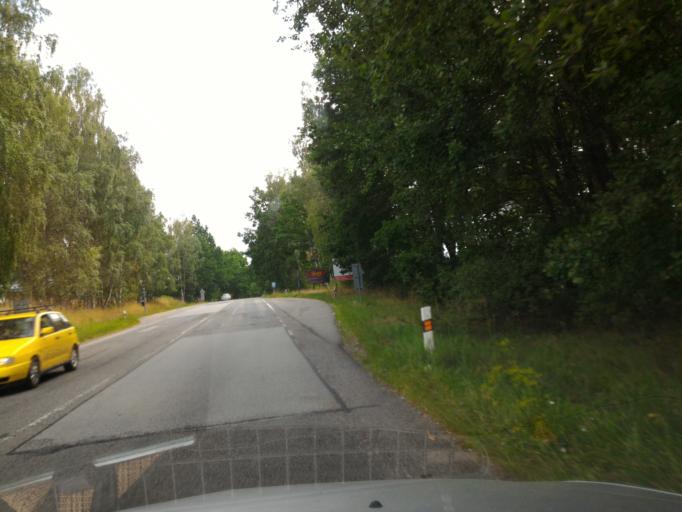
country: CZ
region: Vysocina
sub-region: Okres Jihlava
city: Trest'
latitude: 49.3079
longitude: 15.4814
